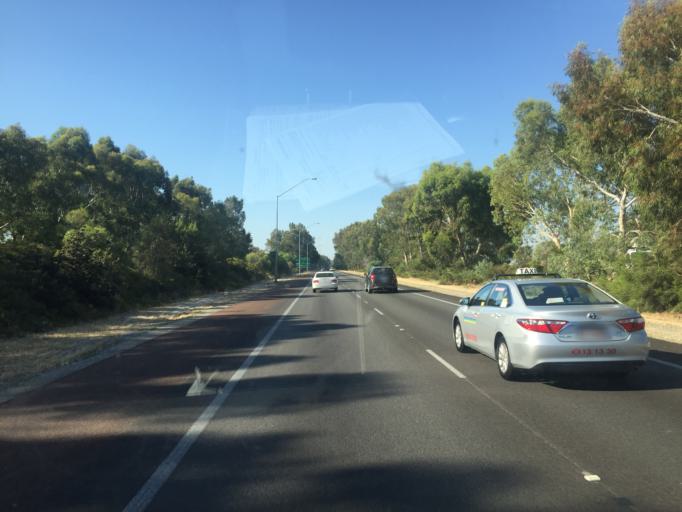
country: AU
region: Western Australia
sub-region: Gosnells
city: Kenwick
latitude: -32.0201
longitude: 115.9719
